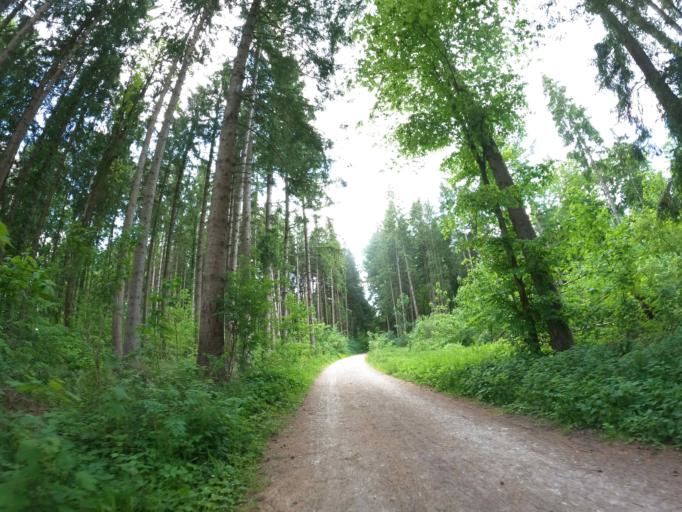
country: DE
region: Bavaria
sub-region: Upper Bavaria
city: Sauerlach
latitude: 47.9940
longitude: 11.6381
